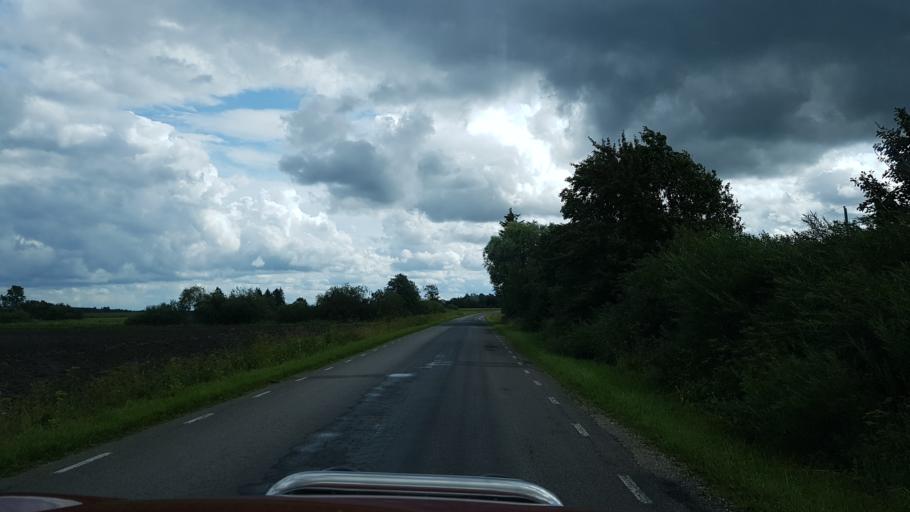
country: EE
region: Laeaene
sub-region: Lihula vald
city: Lihula
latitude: 58.7165
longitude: 23.9919
